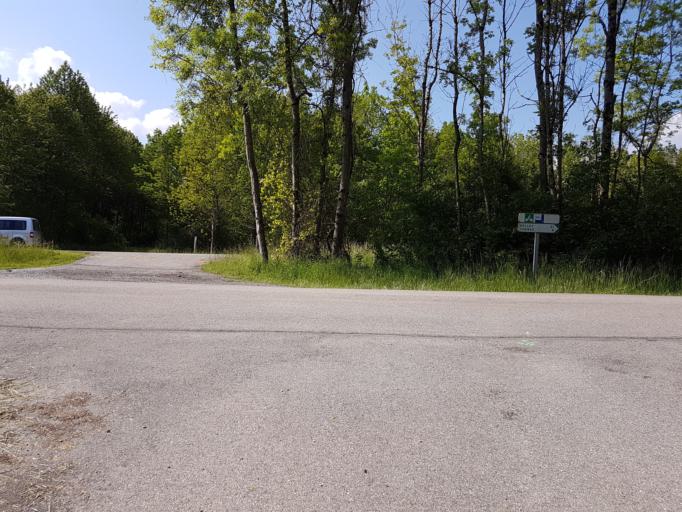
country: FR
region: Rhone-Alpes
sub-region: Departement de l'Ain
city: Culoz
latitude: 45.8517
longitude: 5.8198
